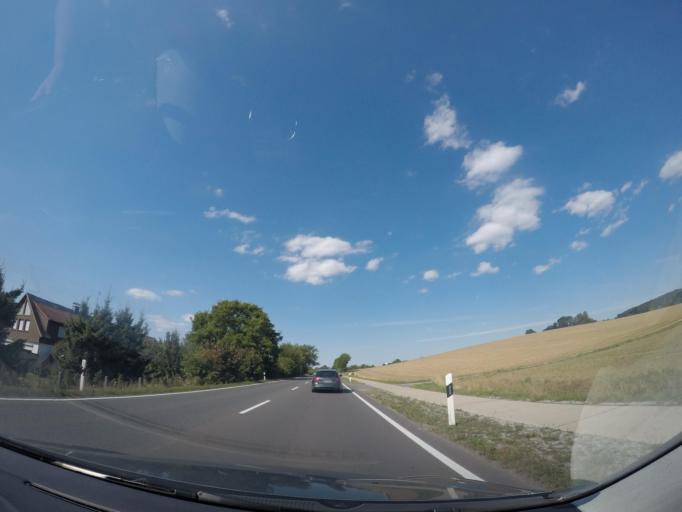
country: DE
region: Lower Saxony
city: Seesen
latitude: 51.8704
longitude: 10.1740
